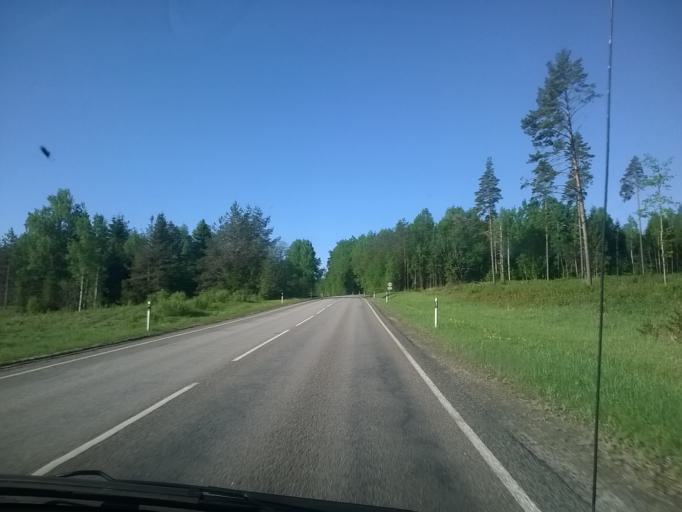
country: EE
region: Valgamaa
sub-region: Valga linn
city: Valga
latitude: 57.9773
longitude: 26.1696
